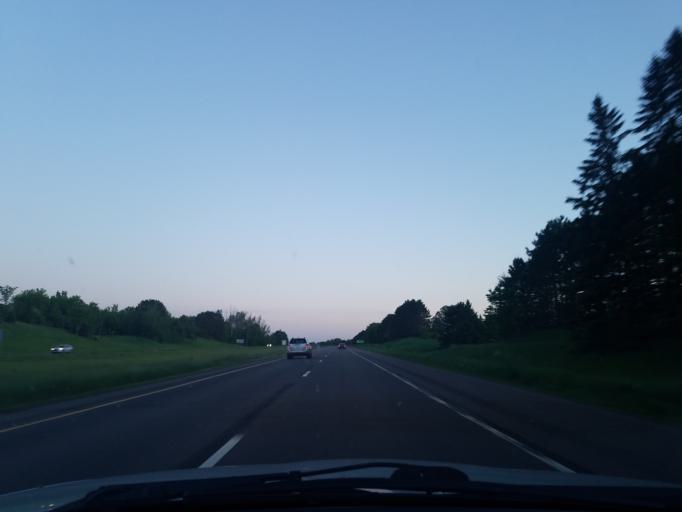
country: US
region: Minnesota
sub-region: Pine County
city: Pine City
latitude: 45.8128
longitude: -92.9862
